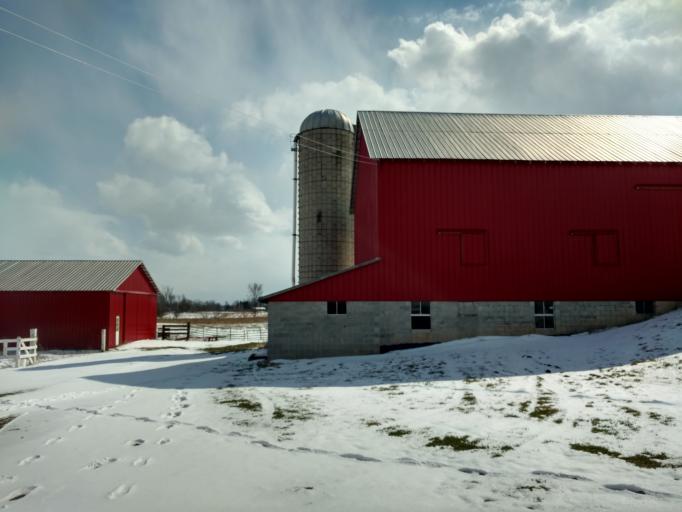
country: US
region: Michigan
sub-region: Gladwin County
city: Gladwin
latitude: 44.0655
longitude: -84.4686
